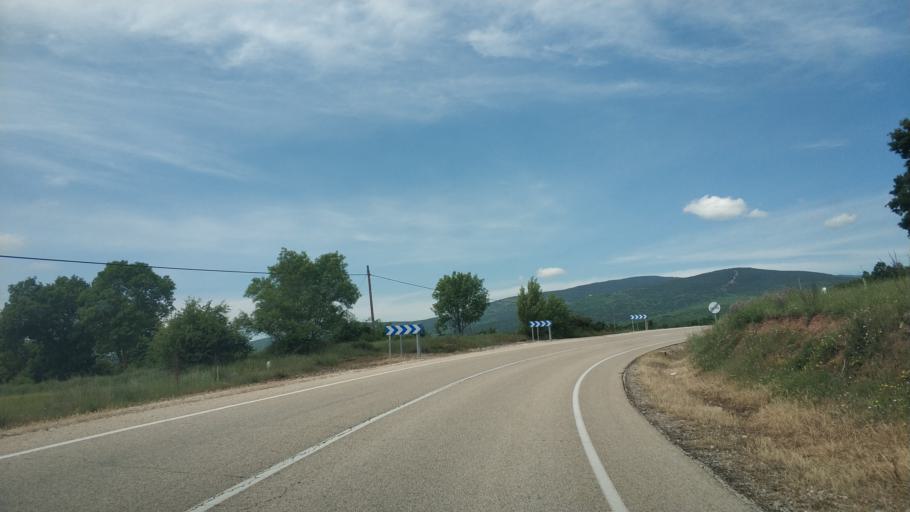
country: ES
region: Castille and Leon
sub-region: Provincia de Soria
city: Sotillo del Rincon
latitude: 41.8898
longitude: -2.6296
